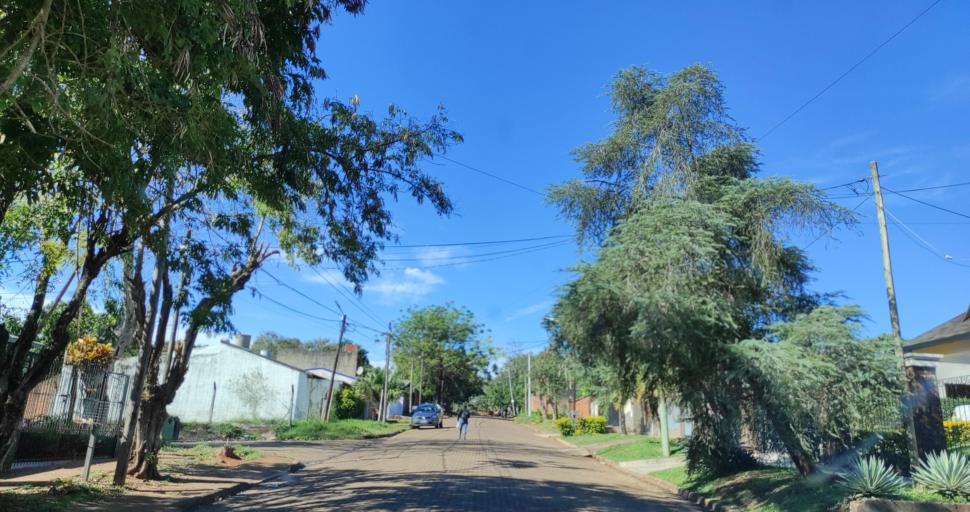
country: AR
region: Misiones
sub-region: Departamento de Capital
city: Posadas
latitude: -27.3661
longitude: -55.9338
